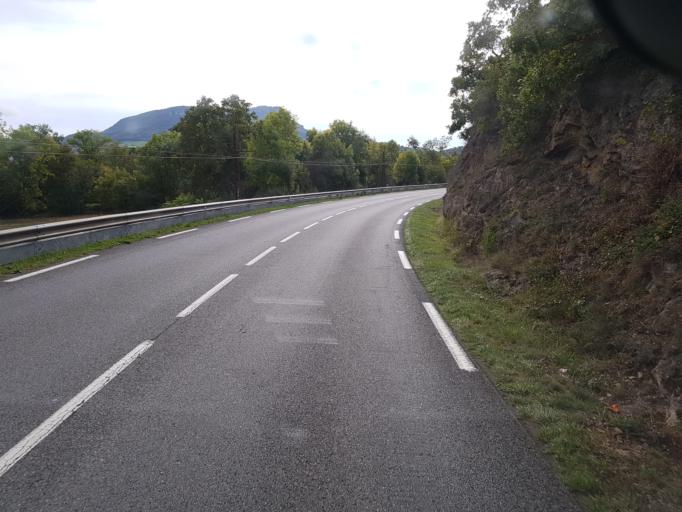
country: FR
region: Midi-Pyrenees
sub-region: Departement de l'Aveyron
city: Saint-Georges-de-Luzencon
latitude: 44.0590
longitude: 2.9818
